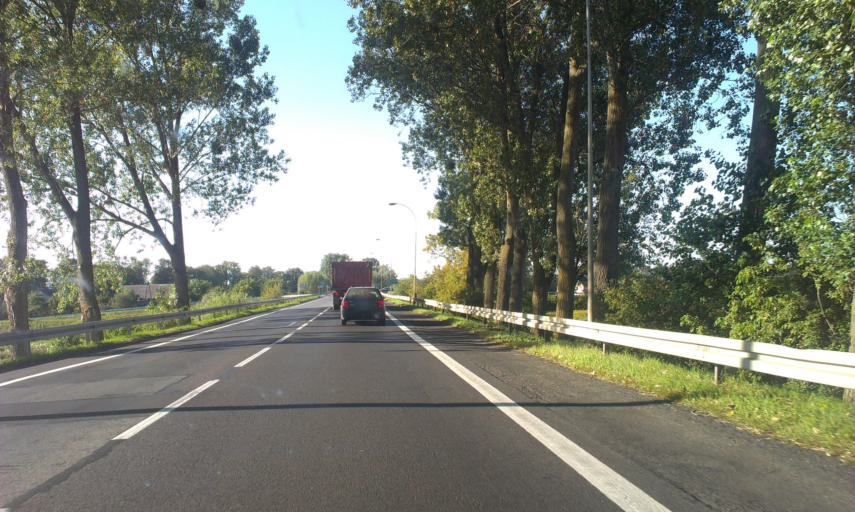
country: PL
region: Kujawsko-Pomorskie
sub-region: Powiat chelminski
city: Chelmno
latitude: 53.3761
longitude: 18.4213
